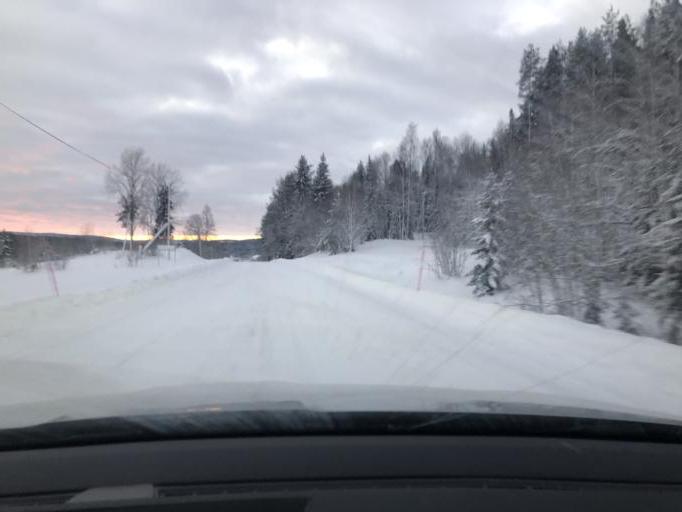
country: SE
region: Vaesternorrland
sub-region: Kramfors Kommun
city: Nordingra
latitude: 62.9271
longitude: 18.1355
